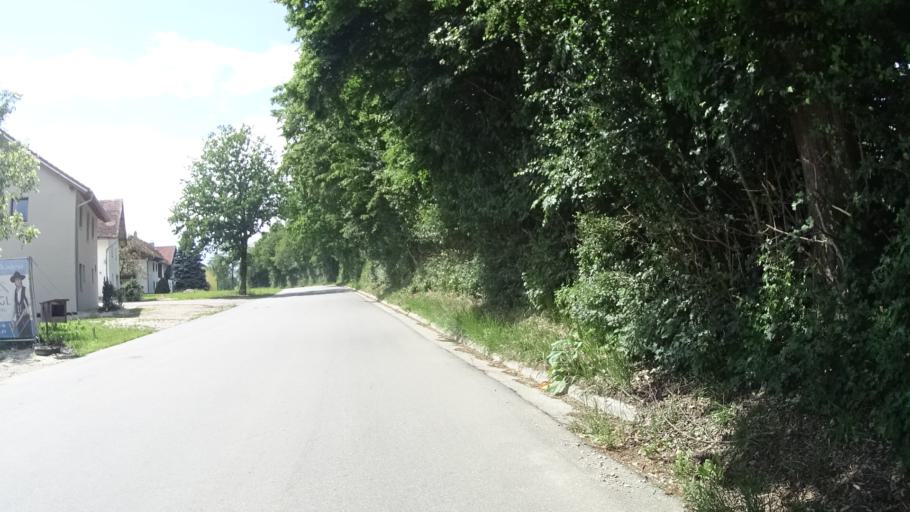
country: DE
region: Bavaria
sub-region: Lower Bavaria
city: Gangkofen
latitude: 48.4428
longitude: 12.5432
